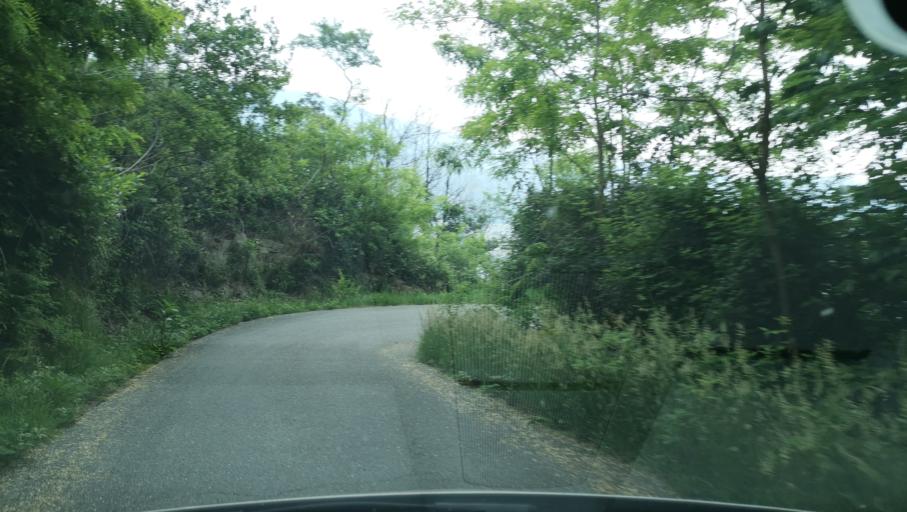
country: IT
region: Piedmont
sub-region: Provincia di Torino
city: Quassolo
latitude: 45.5276
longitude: 7.8266
